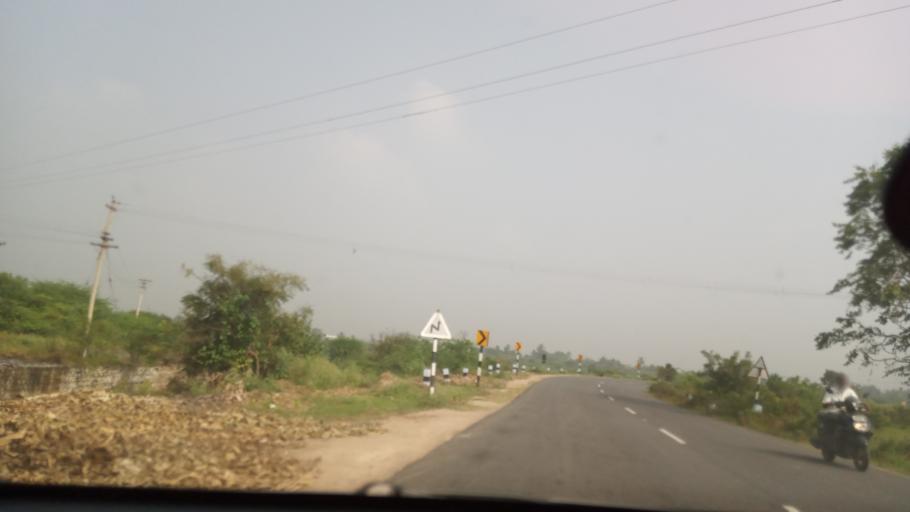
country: IN
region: Tamil Nadu
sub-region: Erode
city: Punjai Puliyampatti
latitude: 11.3934
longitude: 77.1785
